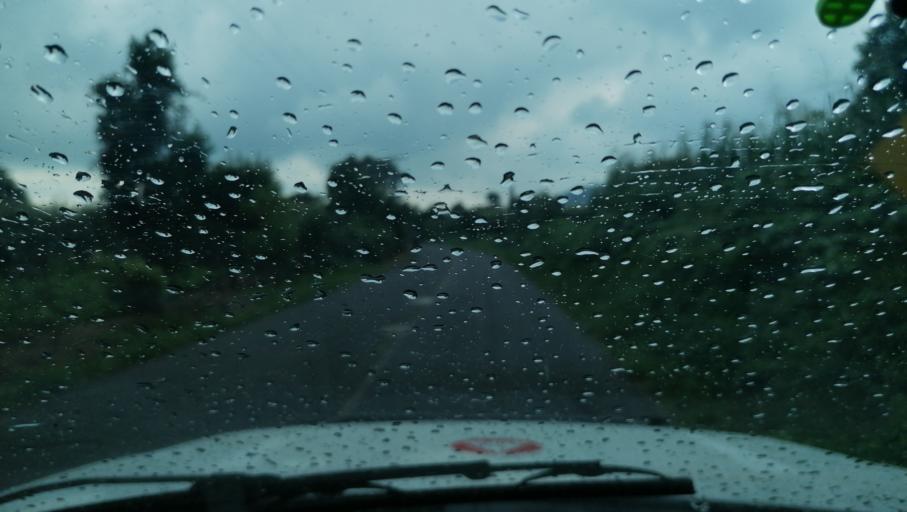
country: MX
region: Morelos
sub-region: Yecapixtla
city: Texcala
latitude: 18.9324
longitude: -98.8049
